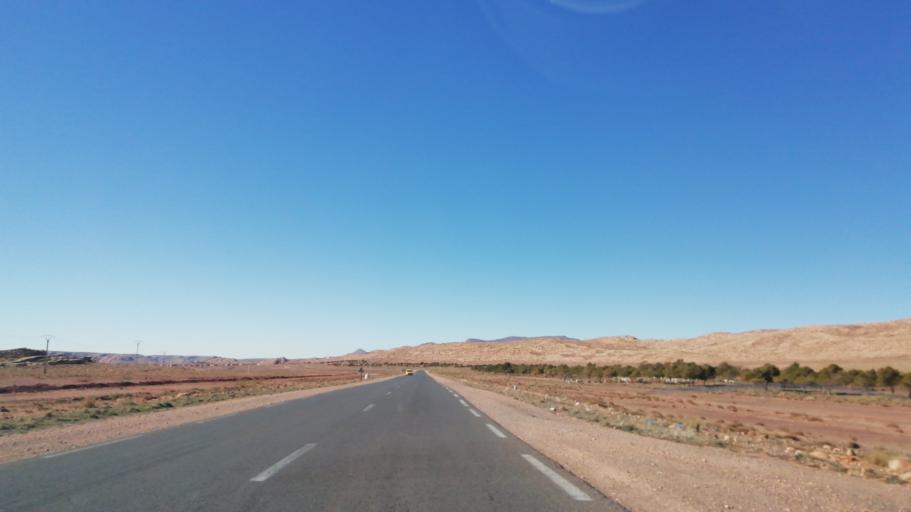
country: DZ
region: El Bayadh
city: El Bayadh
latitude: 33.6176
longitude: 1.1954
